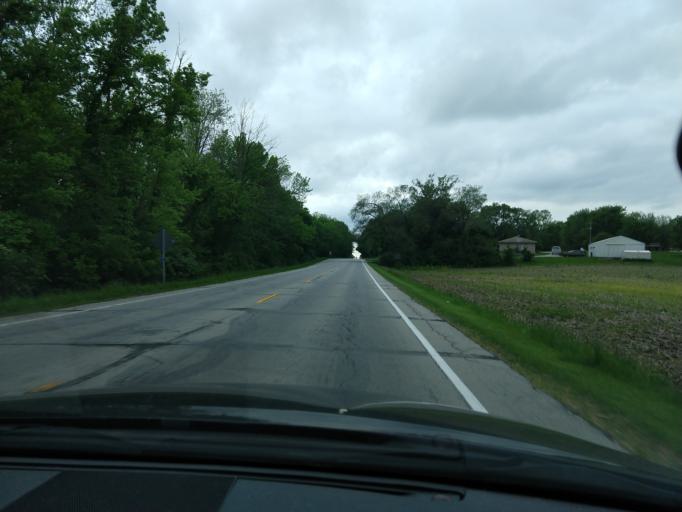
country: US
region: Indiana
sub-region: Hamilton County
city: Noblesville
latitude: 40.0502
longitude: -85.9391
